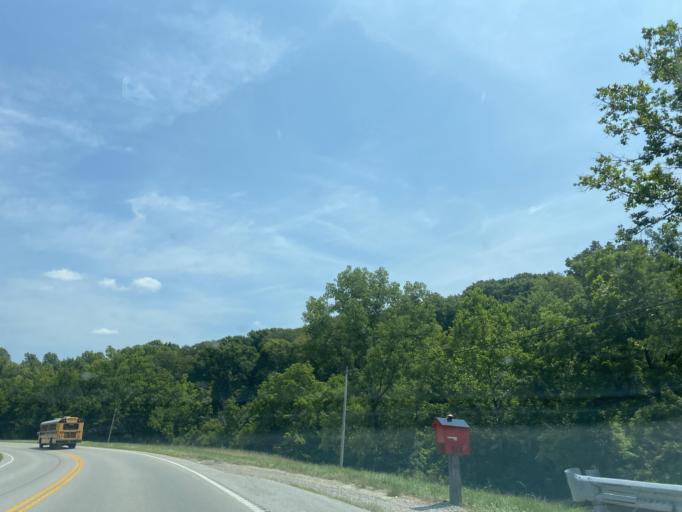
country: US
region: Kentucky
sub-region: Campbell County
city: Claryville
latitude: 38.9322
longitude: -84.4217
